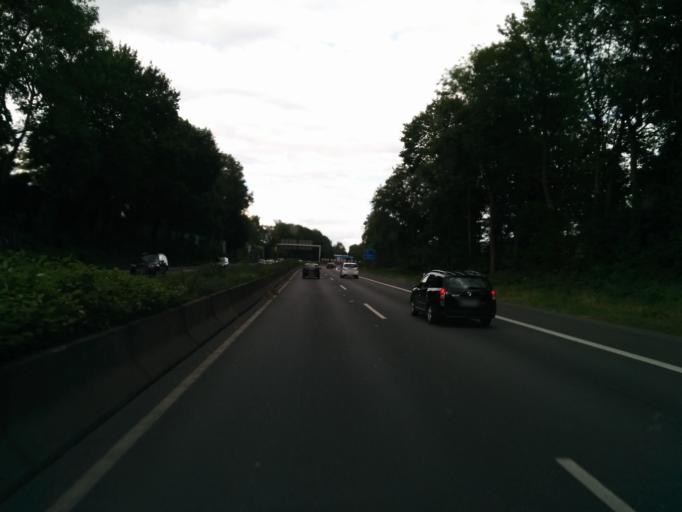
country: DE
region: North Rhine-Westphalia
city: Witten
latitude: 51.4967
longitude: 7.3271
